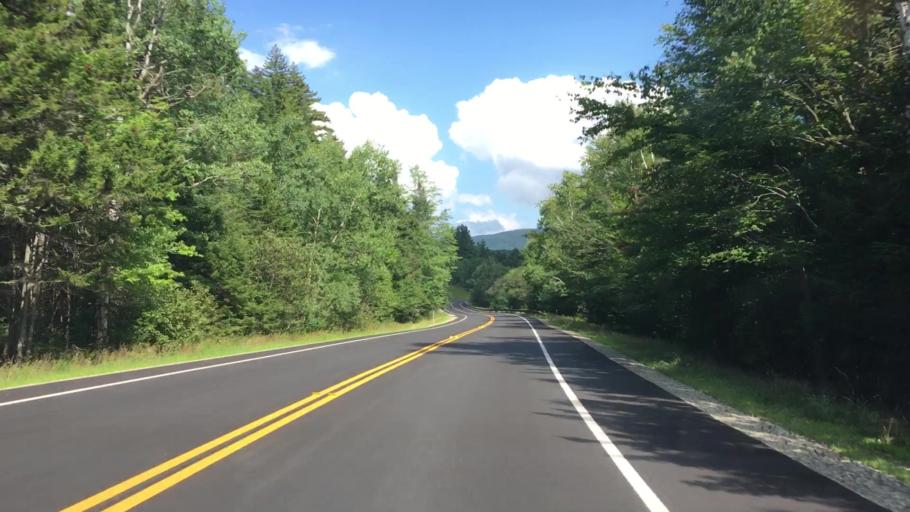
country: US
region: New Hampshire
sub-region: Grafton County
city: North Haverhill
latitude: 44.0982
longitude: -71.8423
